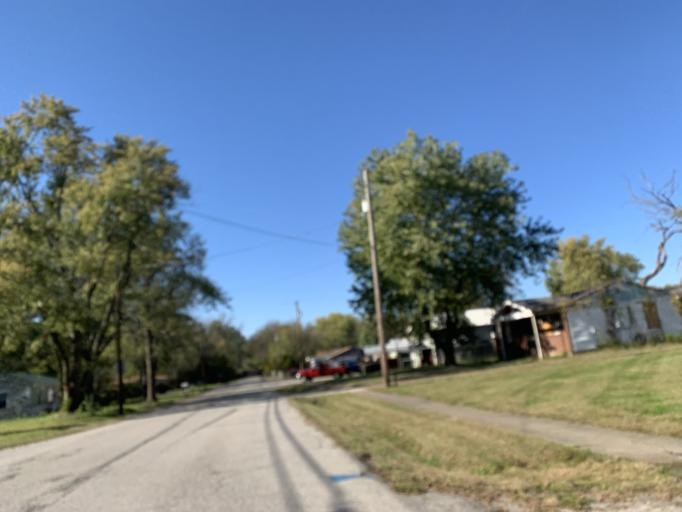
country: US
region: Kentucky
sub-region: Jefferson County
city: Saint Dennis
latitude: 38.1933
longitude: -85.8753
